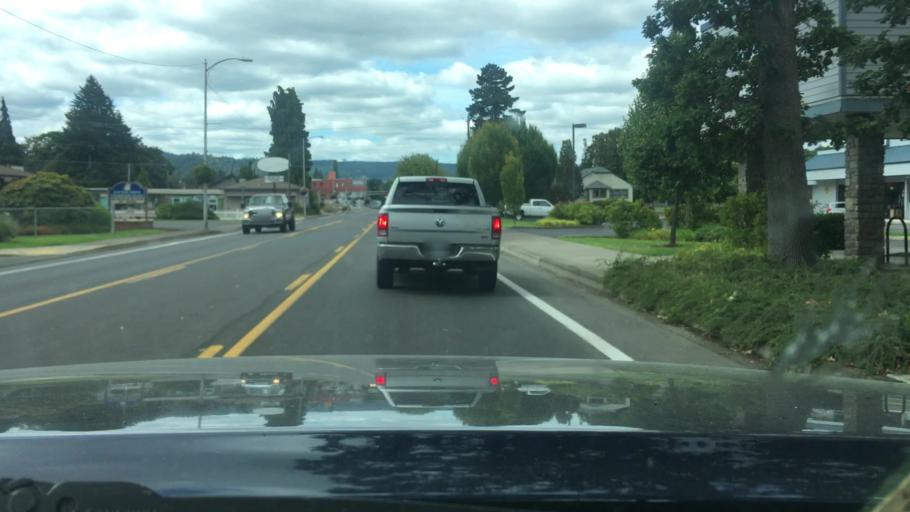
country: US
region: Oregon
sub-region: Lane County
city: Cottage Grove
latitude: 43.7973
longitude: -123.0544
